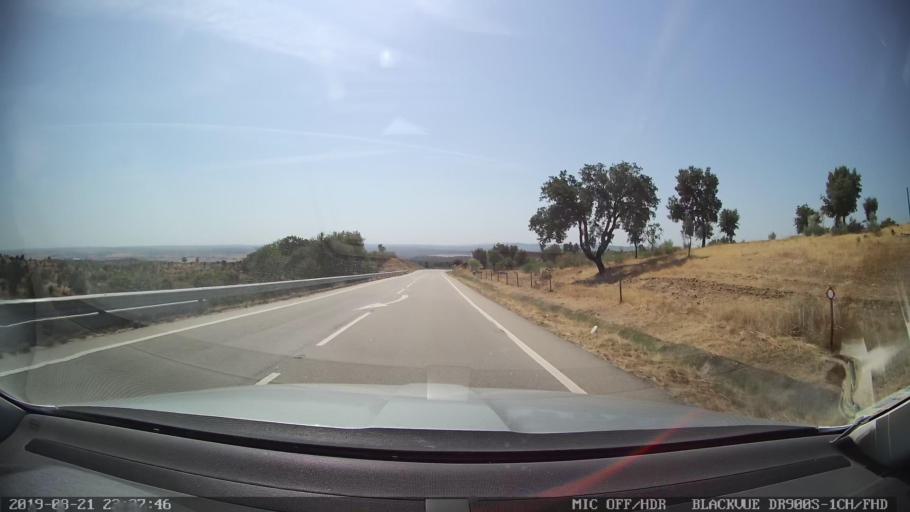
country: PT
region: Guarda
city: Alcains
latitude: 39.8659
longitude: -7.3563
